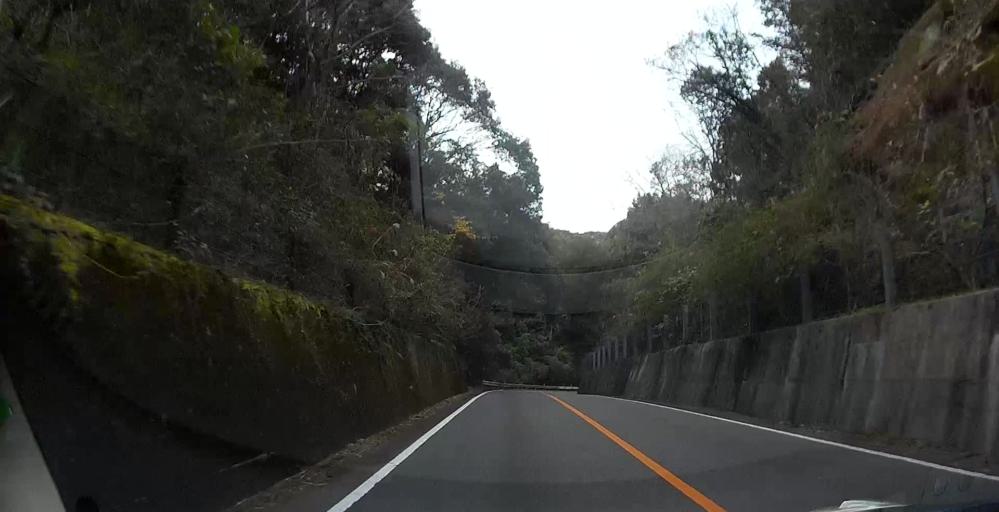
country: JP
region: Kumamoto
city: Hondo
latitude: 32.5051
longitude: 130.3862
